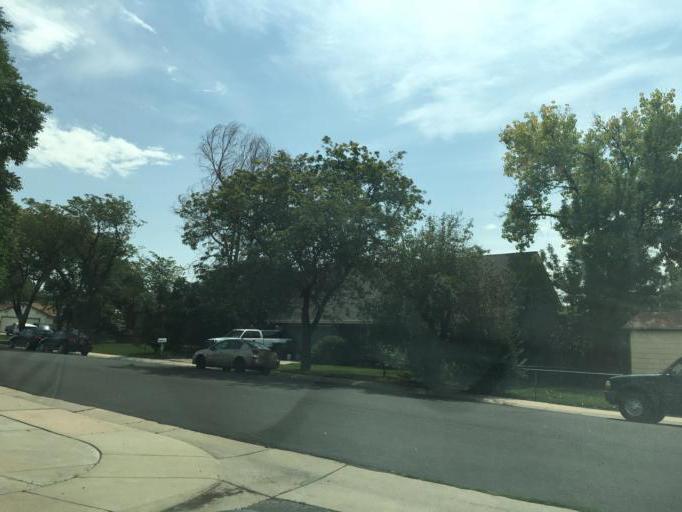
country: US
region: Colorado
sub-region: Adams County
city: Aurora
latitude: 39.7321
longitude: -104.8061
